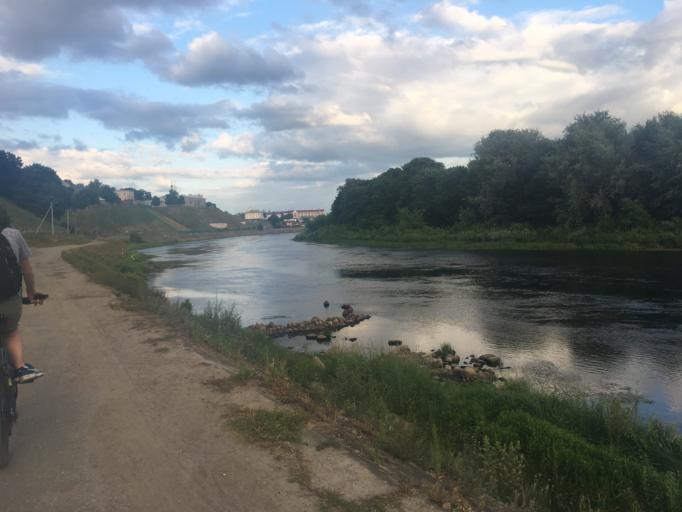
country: BY
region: Grodnenskaya
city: Hrodna
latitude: 53.6786
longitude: 23.8153
